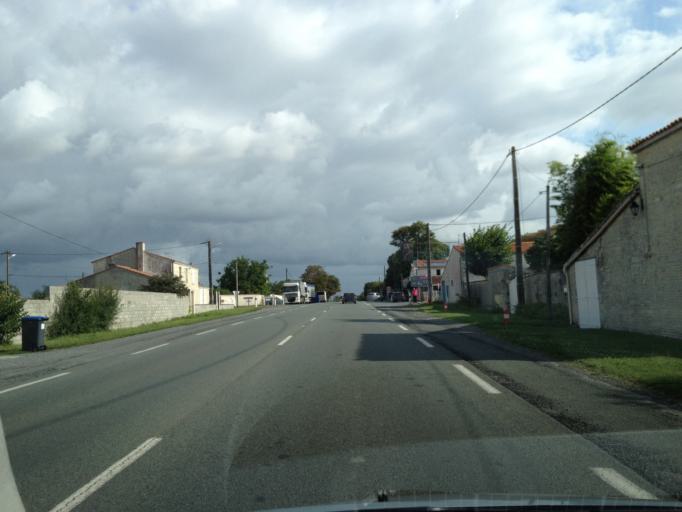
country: FR
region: Poitou-Charentes
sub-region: Departement de la Charente-Maritime
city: Sainte-Soulle
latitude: 46.2071
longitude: -1.0268
